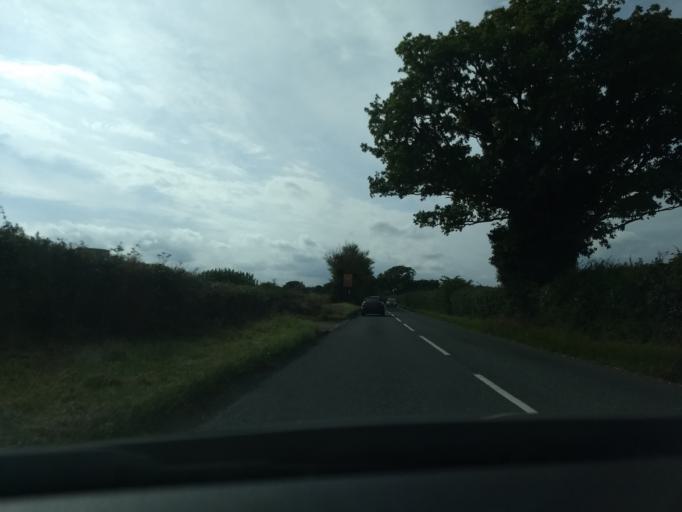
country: GB
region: England
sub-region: Suffolk
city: Ipswich
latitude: 52.0049
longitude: 1.1688
